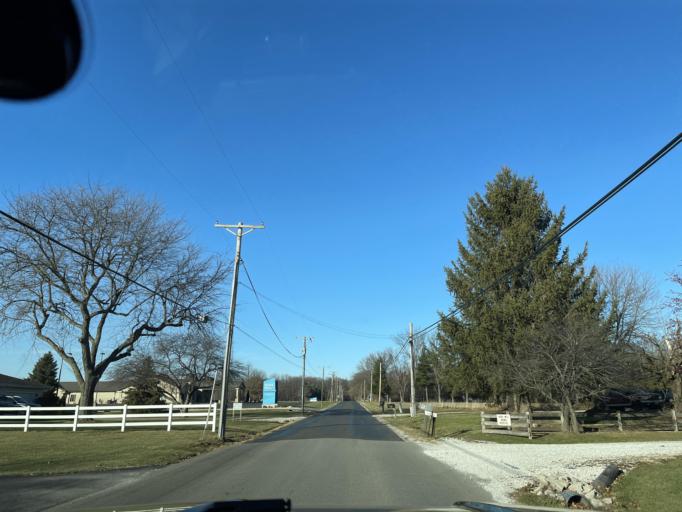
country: US
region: Illinois
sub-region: Sangamon County
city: Leland Grove
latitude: 39.7933
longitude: -89.7154
